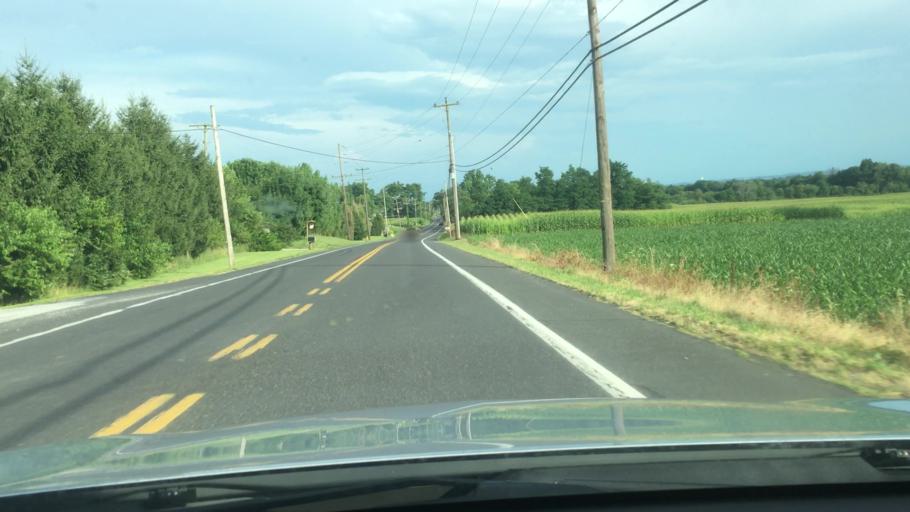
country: US
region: Pennsylvania
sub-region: York County
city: Dover
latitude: 40.0199
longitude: -76.8678
